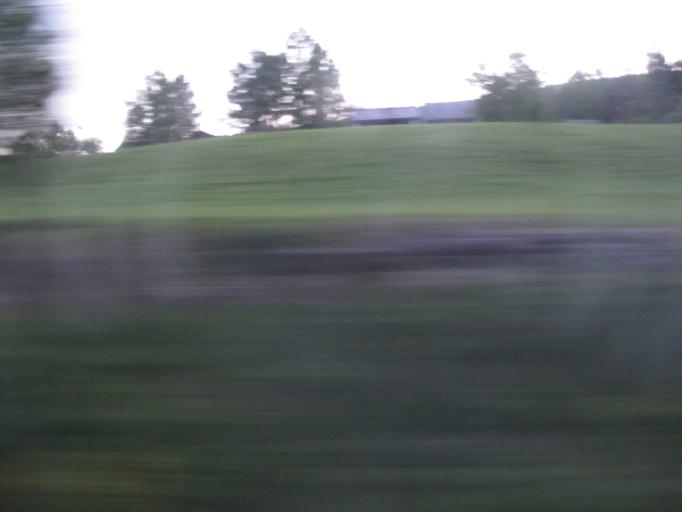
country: NO
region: Oppland
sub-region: Sor-Fron
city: Hundorp
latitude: 61.5466
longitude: 9.9606
